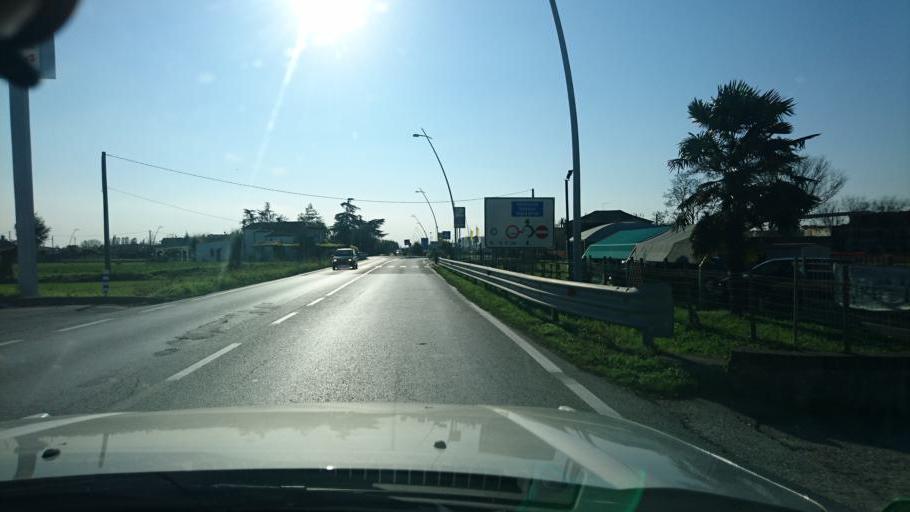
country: IT
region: Veneto
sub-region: Provincia di Padova
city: Monselice
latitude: 45.2185
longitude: 11.7552
